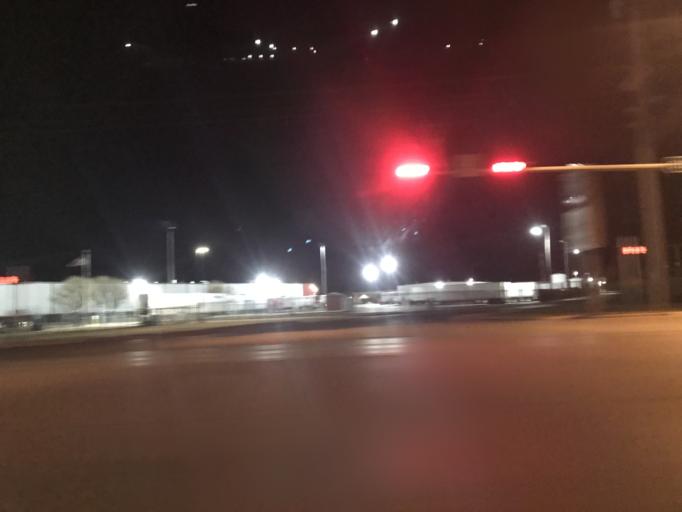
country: US
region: Texas
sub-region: Taylor County
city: Abilene
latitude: 32.4800
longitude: -99.6943
